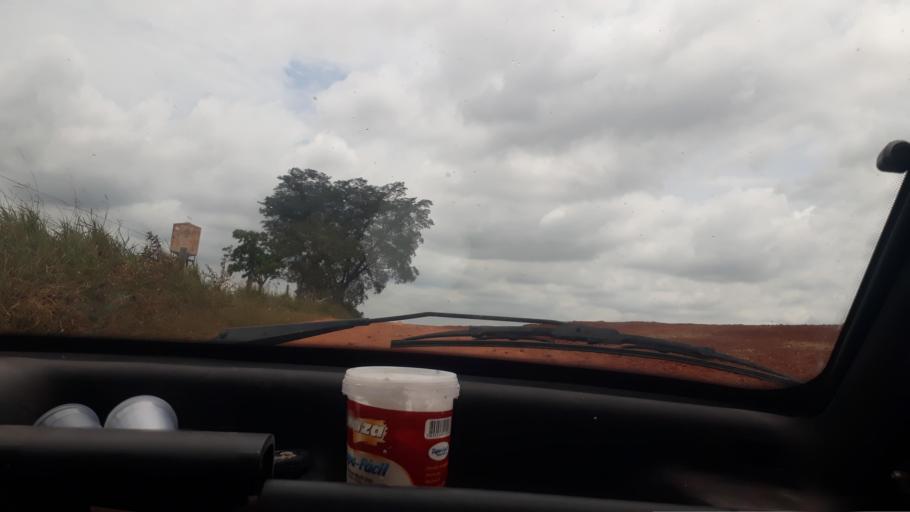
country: BR
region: Sao Paulo
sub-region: Regente Feijo
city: Regente Feijo
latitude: -22.2547
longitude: -51.3000
